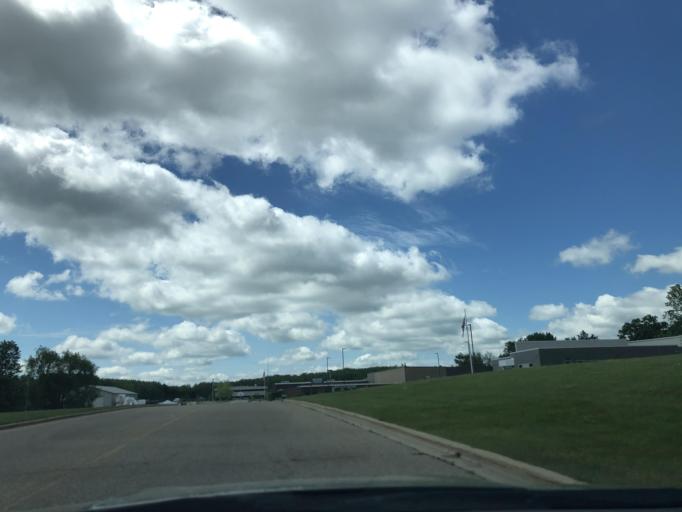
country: US
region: Michigan
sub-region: Clare County
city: Harrison
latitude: 44.0186
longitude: -84.8118
